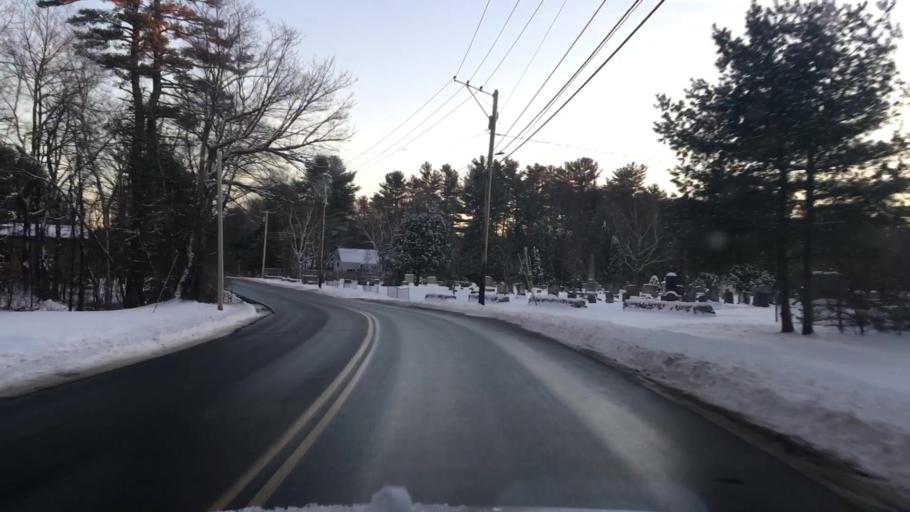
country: US
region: Maine
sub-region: Cumberland County
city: Brunswick
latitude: 43.9514
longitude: -69.9304
